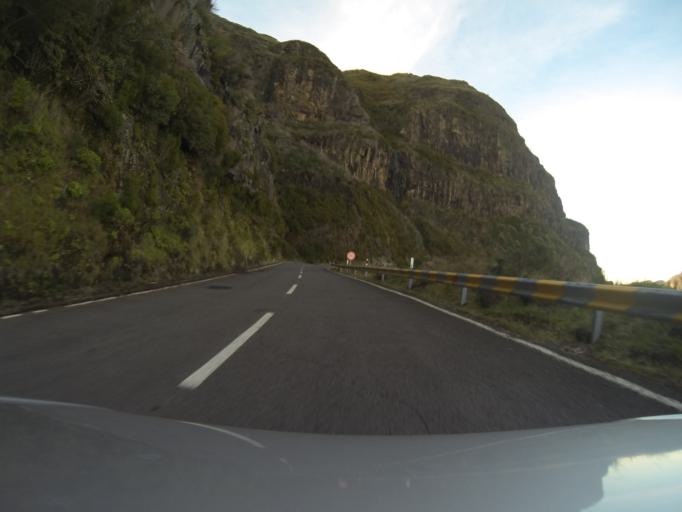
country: PT
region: Madeira
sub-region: Sao Vicente
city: Sao Vicente
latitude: 32.7417
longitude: -17.0465
